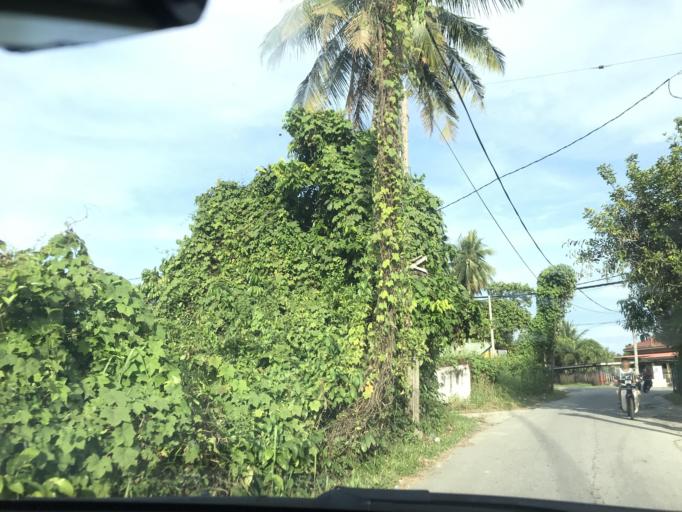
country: MY
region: Kelantan
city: Kota Bharu
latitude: 6.1278
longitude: 102.2219
